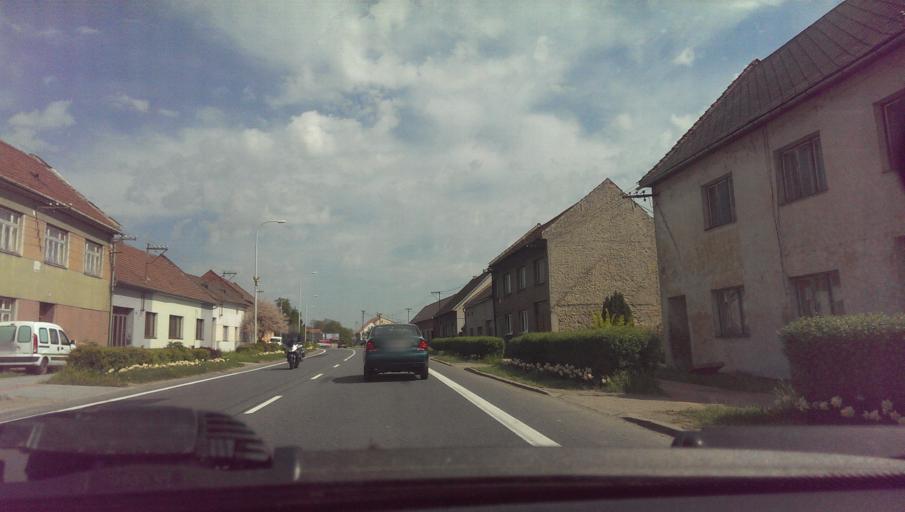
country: CZ
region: Zlin
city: Spytihnev
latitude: 49.1429
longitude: 17.4990
